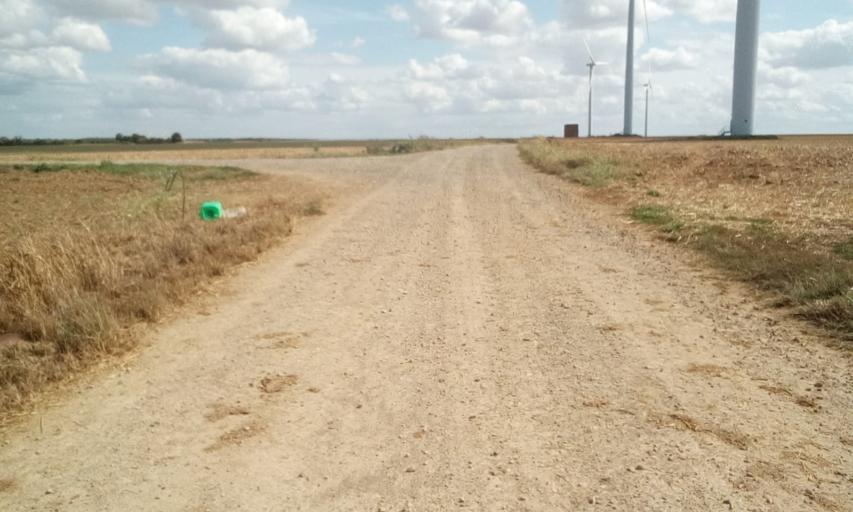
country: FR
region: Lower Normandy
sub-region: Departement du Calvados
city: Bellengreville
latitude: 49.1015
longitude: -0.2318
